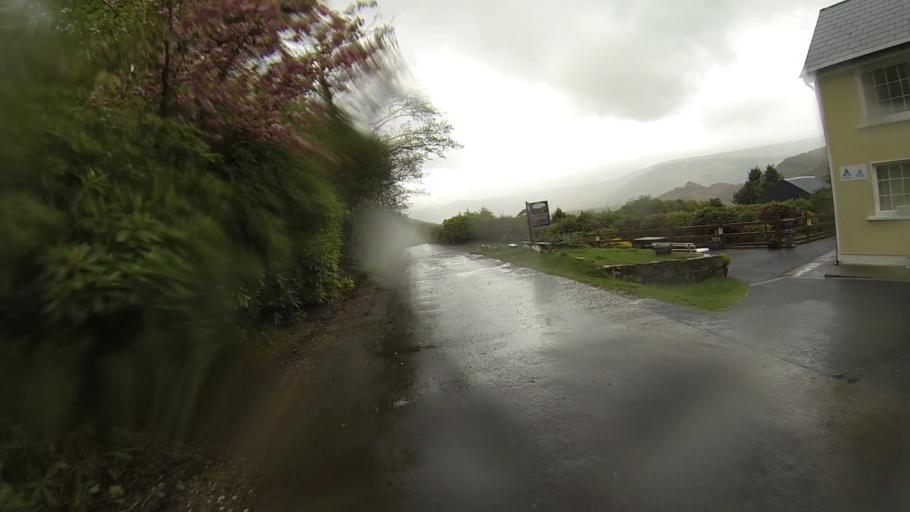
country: IE
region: Munster
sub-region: Ciarrai
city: Kenmare
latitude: 51.9867
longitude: -9.6519
